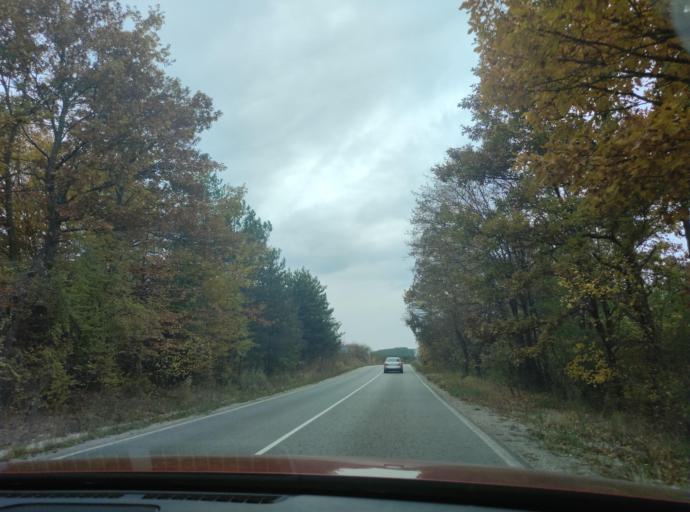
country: BG
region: Sofiya
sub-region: Obshtina Godech
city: Godech
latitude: 42.9806
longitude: 23.1332
